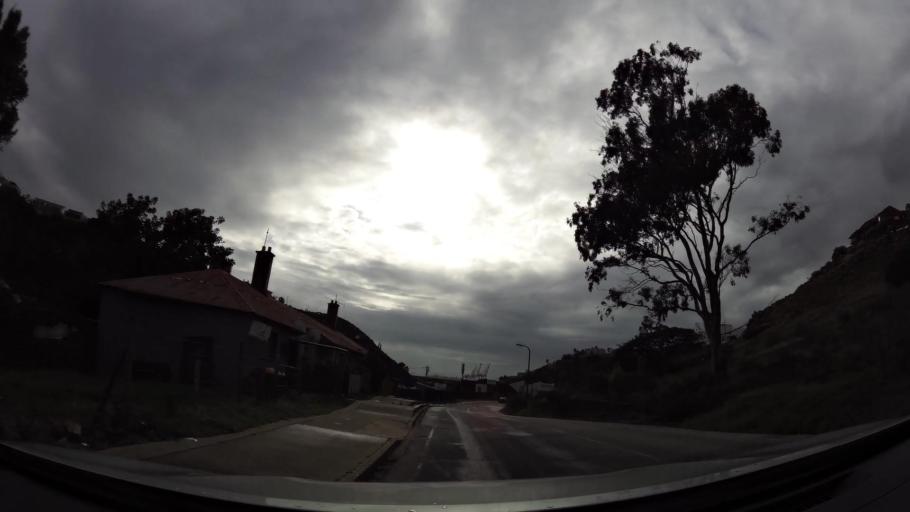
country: ZA
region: Eastern Cape
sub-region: Nelson Mandela Bay Metropolitan Municipality
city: Port Elizabeth
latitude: -33.9697
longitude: 25.6193
